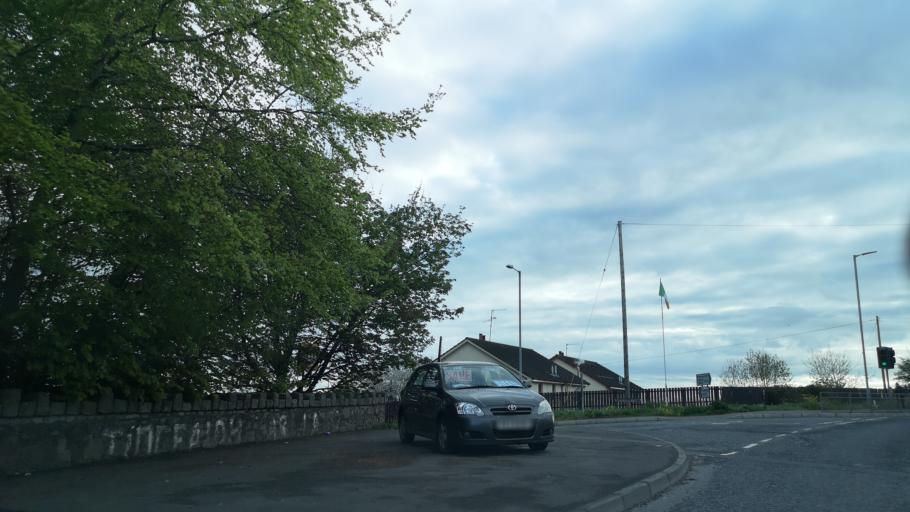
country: GB
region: Northern Ireland
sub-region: Newry and Mourne District
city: Newry
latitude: 54.1874
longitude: -6.3775
